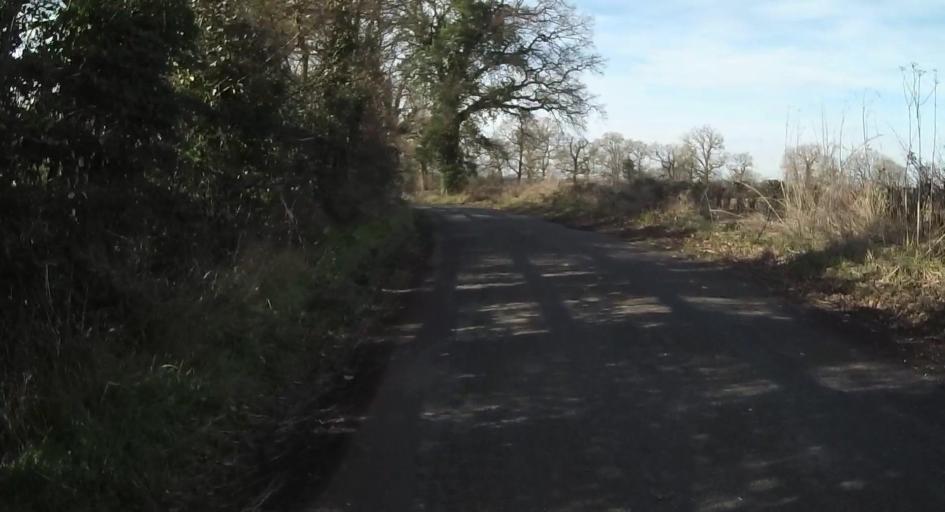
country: GB
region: England
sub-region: West Berkshire
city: Stratfield Mortimer
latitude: 51.3747
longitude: -1.0011
